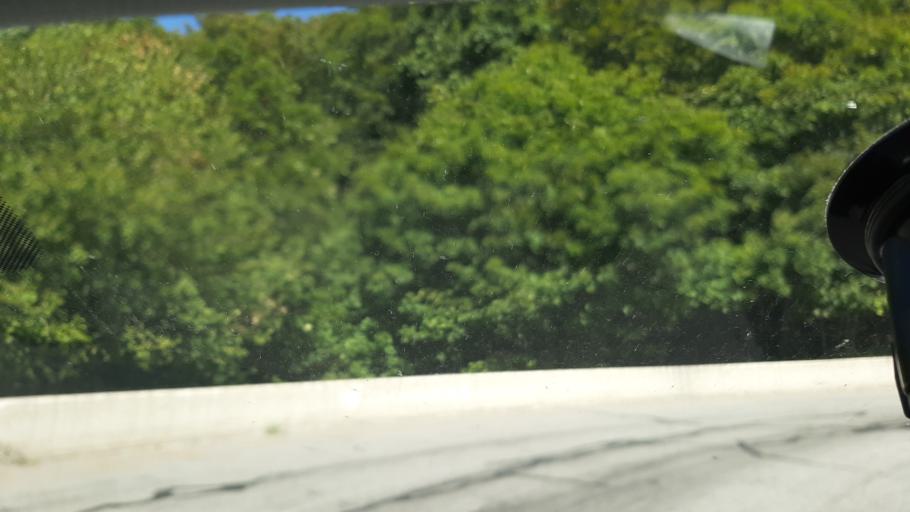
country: FR
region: Rhone-Alpes
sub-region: Departement de la Savoie
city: Saint-Michel-de-Maurienne
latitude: 45.1822
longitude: 6.4848
